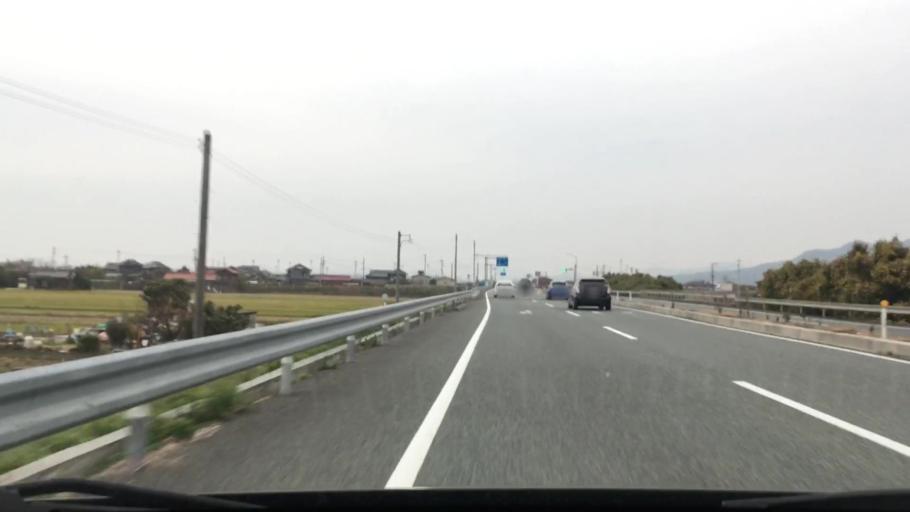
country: JP
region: Yamaguchi
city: Shimonoseki
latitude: 34.0550
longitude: 131.0284
